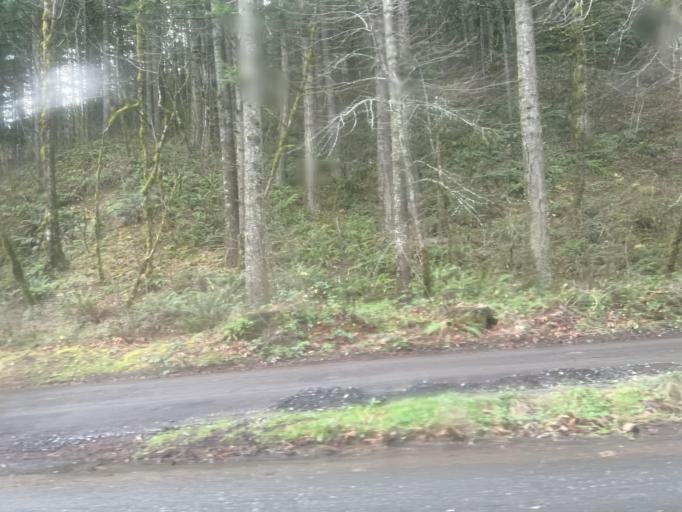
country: US
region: Washington
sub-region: Clark County
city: Washougal
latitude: 45.5528
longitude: -122.1844
